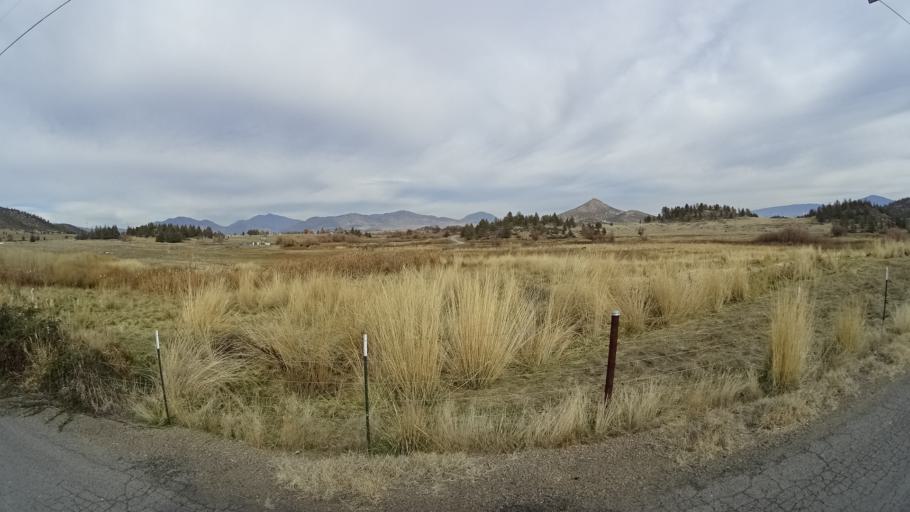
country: US
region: California
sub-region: Siskiyou County
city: Montague
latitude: 41.6833
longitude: -122.5299
